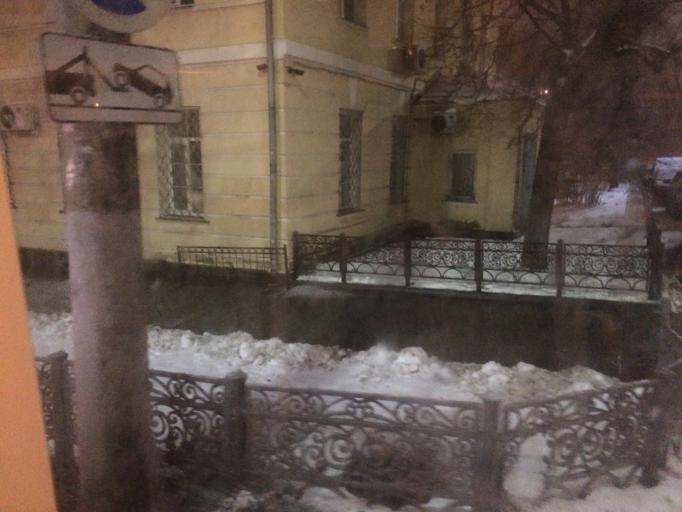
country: RU
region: Tula
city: Tula
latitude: 54.1867
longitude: 37.6106
